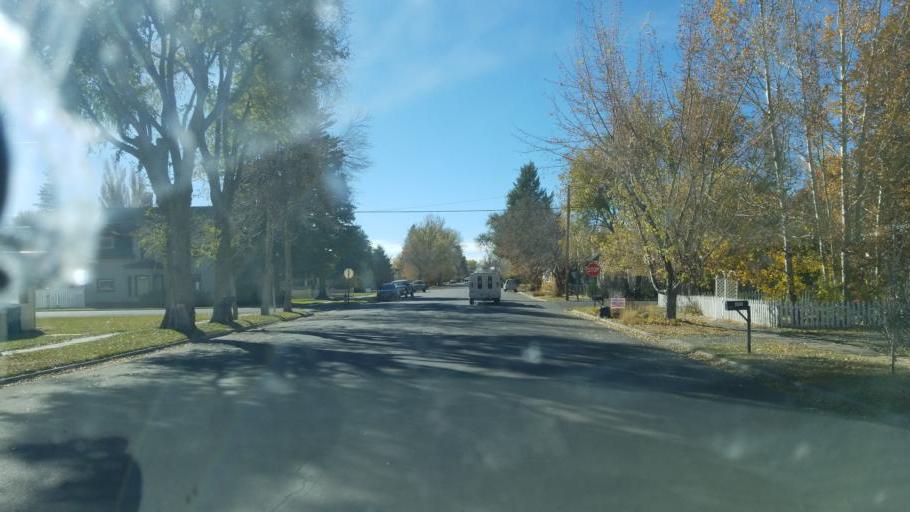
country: US
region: Colorado
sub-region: Rio Grande County
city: Monte Vista
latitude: 37.5771
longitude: -106.1468
